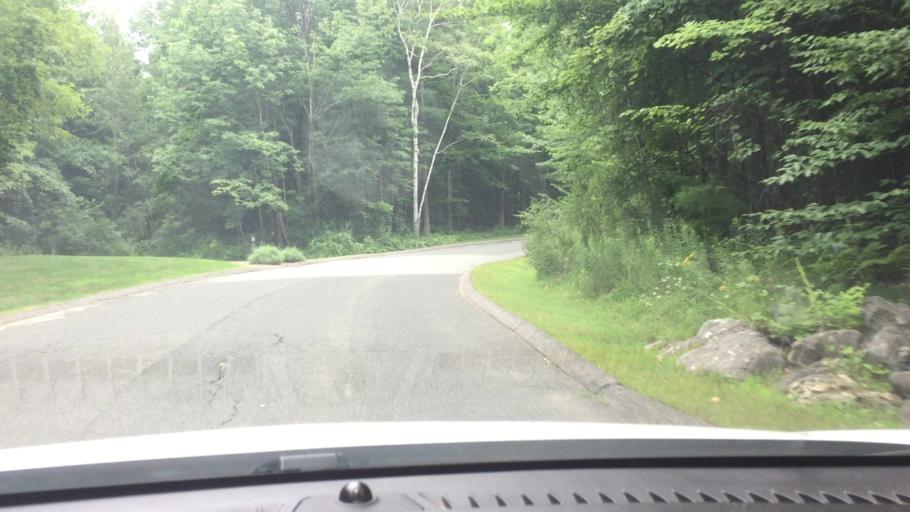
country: US
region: Massachusetts
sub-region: Berkshire County
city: Lenox
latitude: 42.3467
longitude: -73.2636
